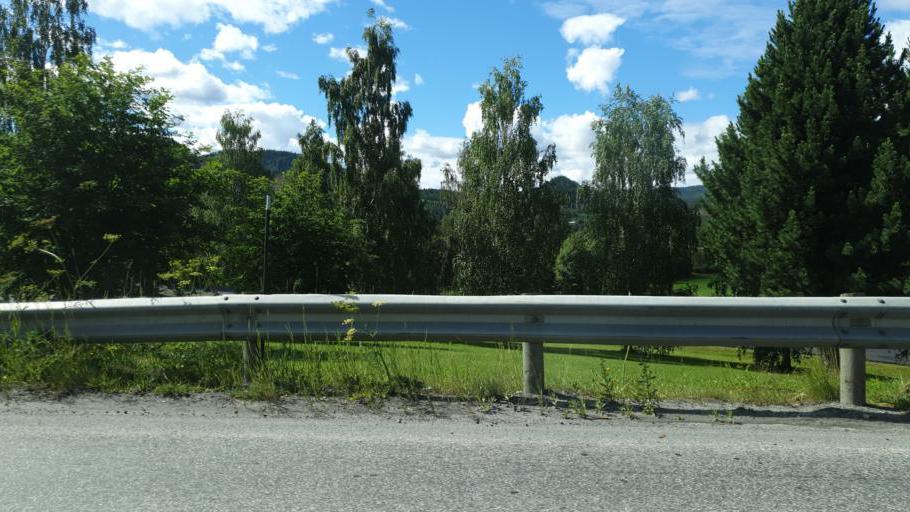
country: NO
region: Sor-Trondelag
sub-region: Midtre Gauldal
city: Storen
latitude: 63.0343
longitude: 10.2928
